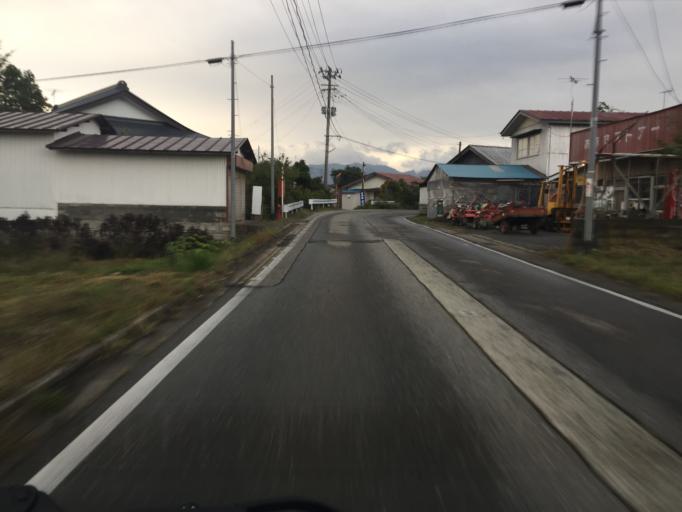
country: JP
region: Fukushima
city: Kitakata
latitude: 37.5030
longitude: 139.8824
